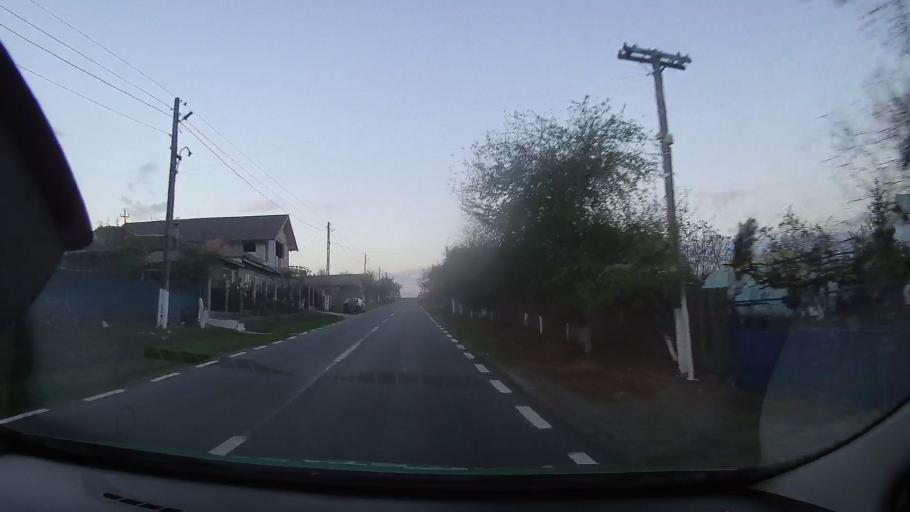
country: RO
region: Constanta
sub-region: Comuna Baneasa
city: Baneasa
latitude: 44.1008
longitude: 27.6765
